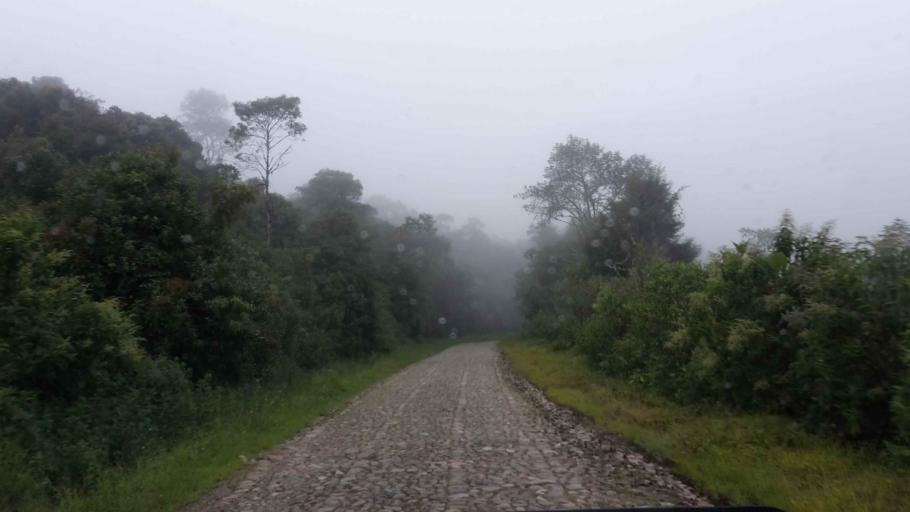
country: BO
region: Cochabamba
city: Colomi
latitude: -17.1305
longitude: -65.9500
